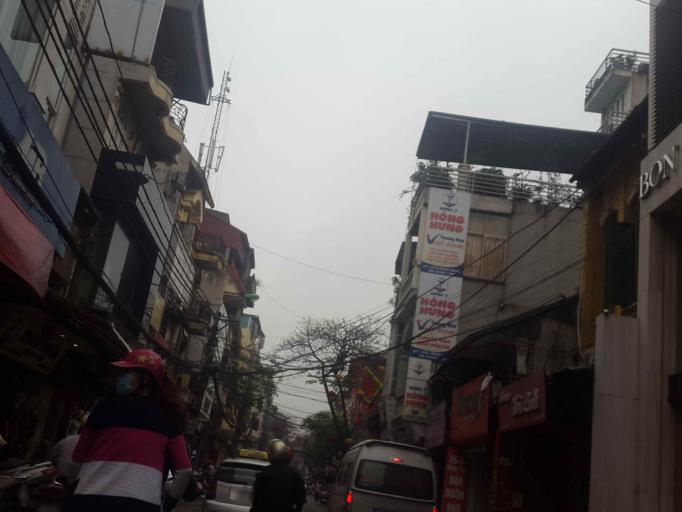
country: VN
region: Ha Noi
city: Hoan Kiem
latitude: 21.0348
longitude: 105.8496
